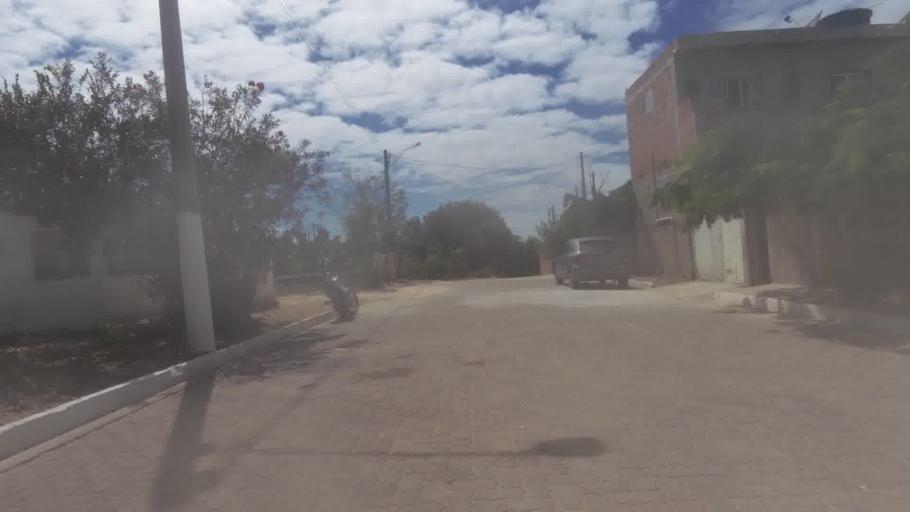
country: BR
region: Espirito Santo
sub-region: Marataizes
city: Marataizes
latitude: -21.1877
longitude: -40.9302
